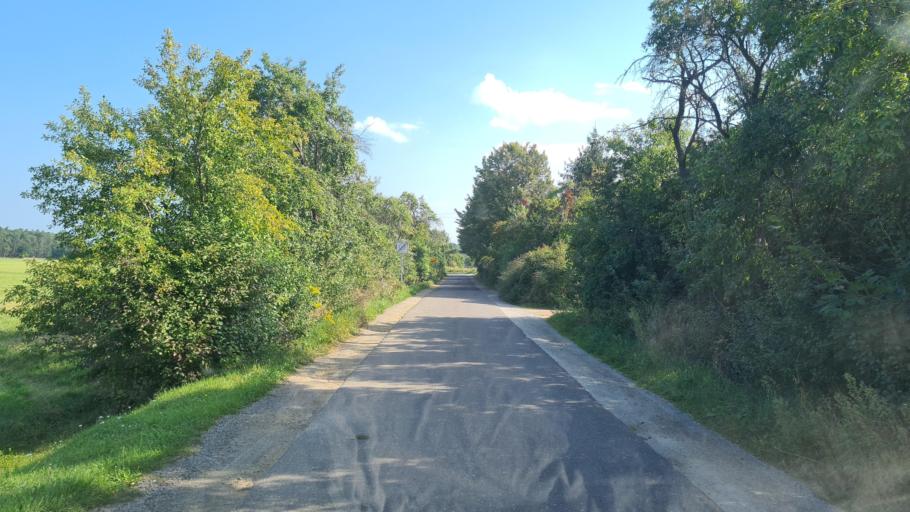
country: DE
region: Brandenburg
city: Kolkwitz
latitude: 51.7008
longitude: 14.2581
